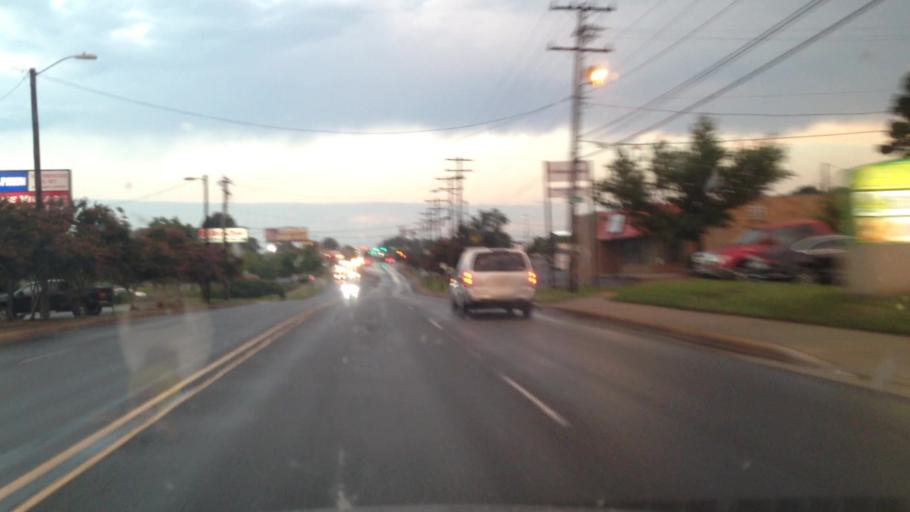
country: US
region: North Carolina
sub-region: Mecklenburg County
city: Pineville
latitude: 35.1491
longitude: -80.8764
